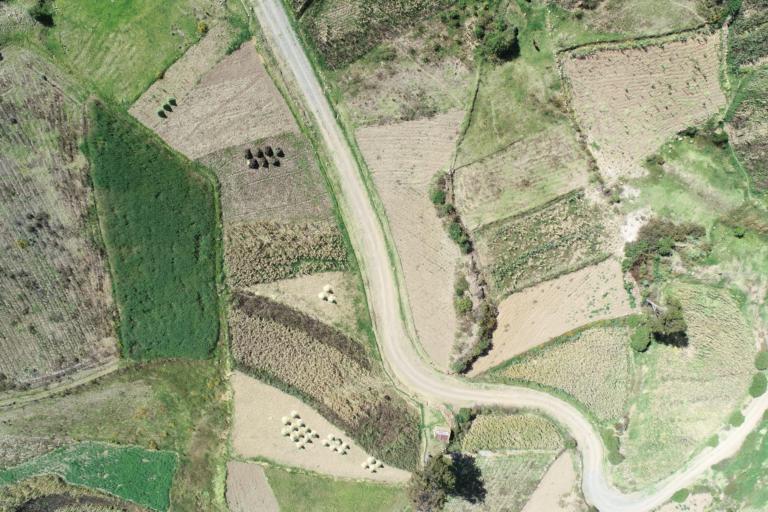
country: BO
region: La Paz
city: La Paz
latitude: -16.5537
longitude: -67.9894
